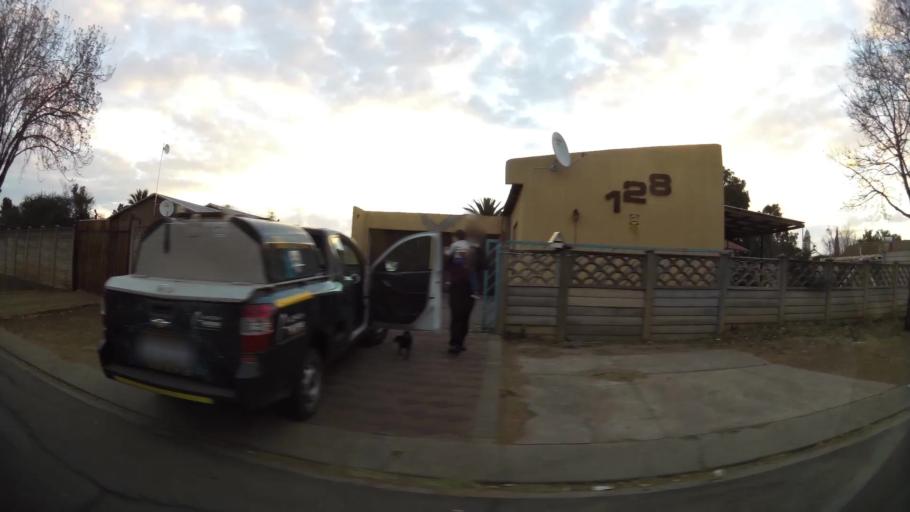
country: ZA
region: Orange Free State
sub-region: Mangaung Metropolitan Municipality
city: Bloemfontein
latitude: -29.1724
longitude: 26.1916
